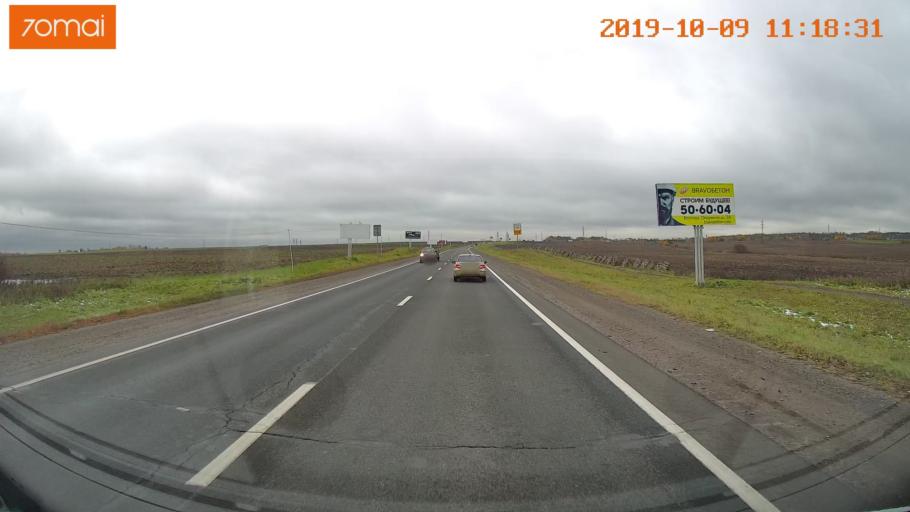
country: RU
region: Vologda
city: Vologda
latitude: 59.1671
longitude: 39.9169
